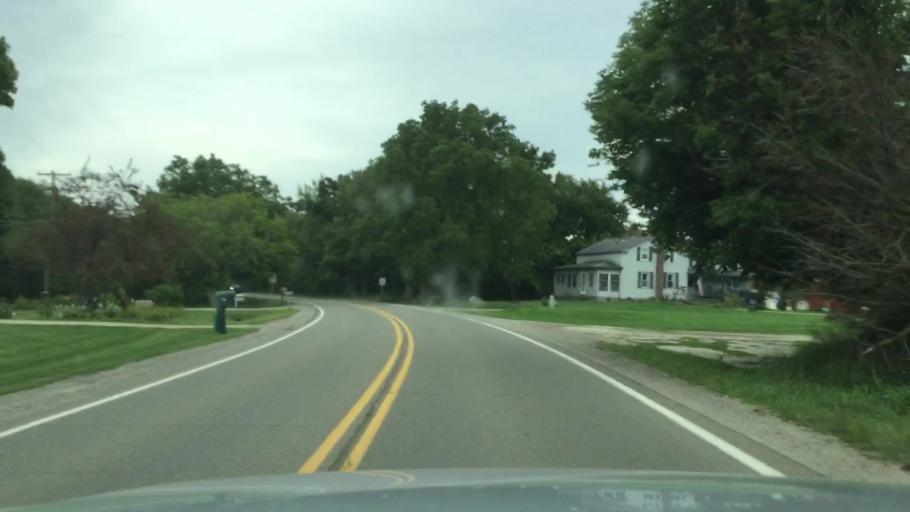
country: US
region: Michigan
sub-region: Genesee County
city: Argentine
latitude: 42.7929
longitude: -83.8521
